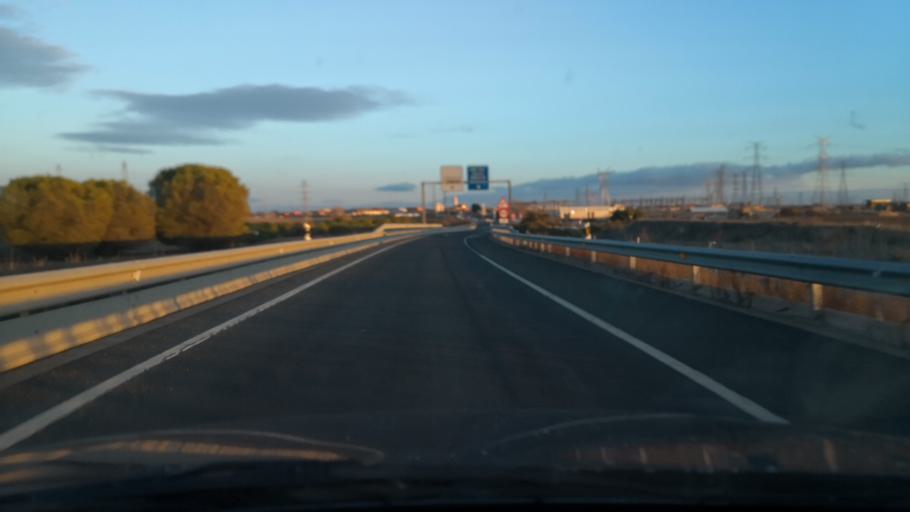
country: ES
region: Castille and Leon
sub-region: Provincia de Valladolid
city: Tordesillas
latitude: 41.5125
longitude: -5.0206
